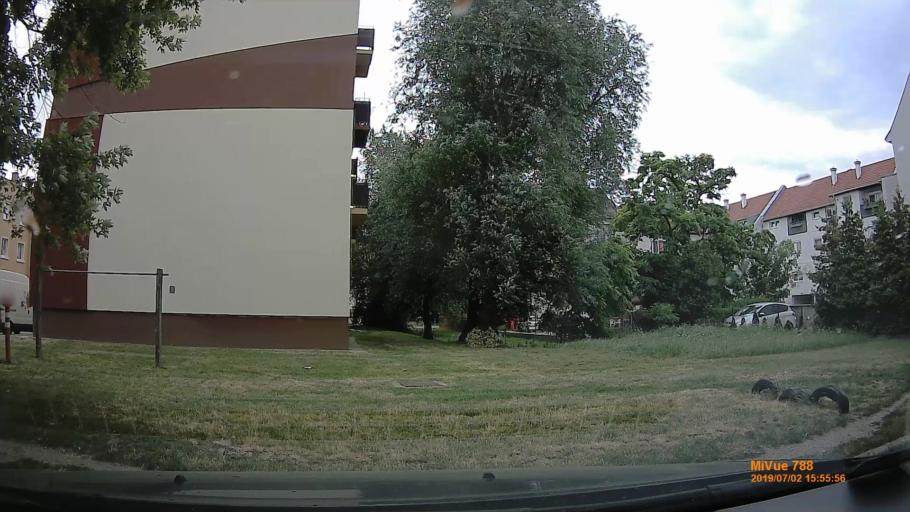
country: HU
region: Gyor-Moson-Sopron
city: Mosonmagyarovar
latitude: 47.8800
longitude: 17.2600
